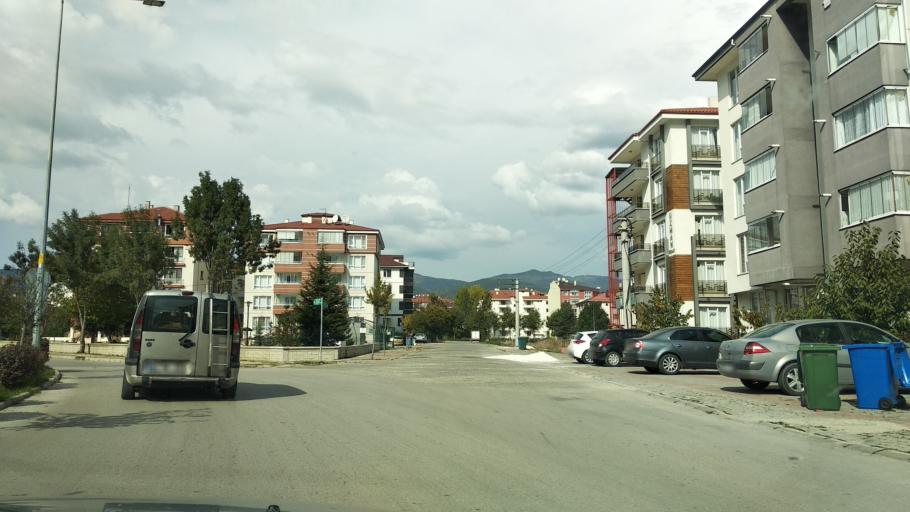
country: TR
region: Bolu
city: Bolu
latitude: 40.7286
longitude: 31.5876
